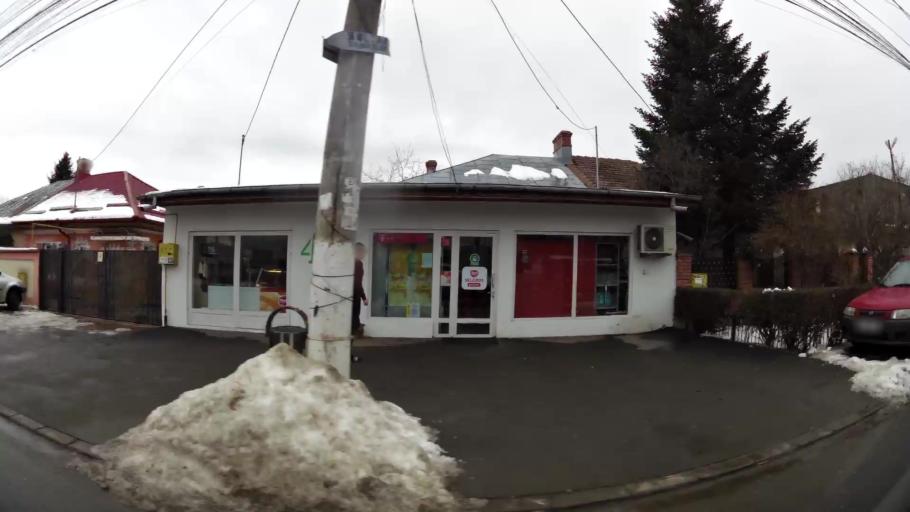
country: RO
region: Ilfov
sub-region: Comuna Pantelimon
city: Pantelimon
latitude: 44.4509
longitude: 26.1985
